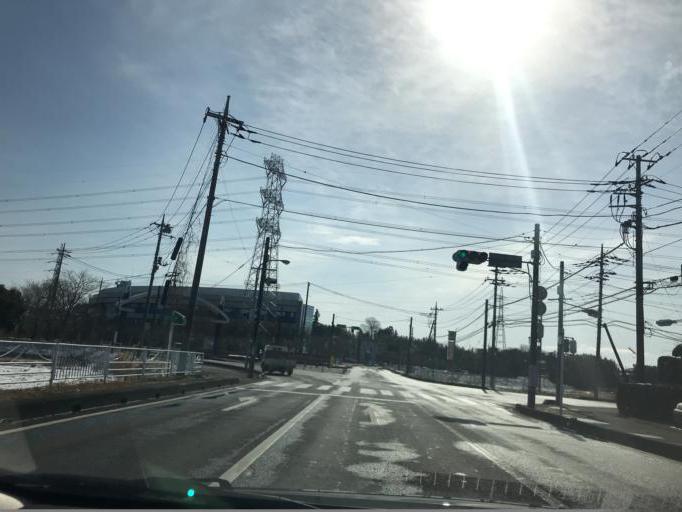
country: JP
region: Ibaraki
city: Moriya
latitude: 35.9575
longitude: 139.9541
